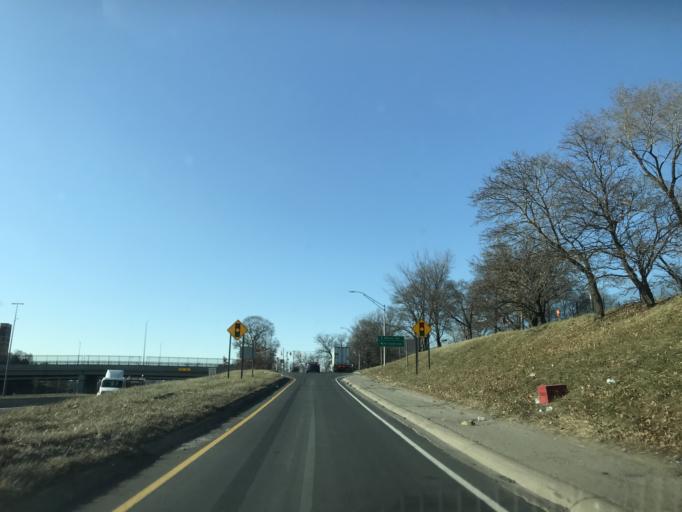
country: US
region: Michigan
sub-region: Wayne County
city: Highland Park
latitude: 42.3477
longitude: -83.1077
